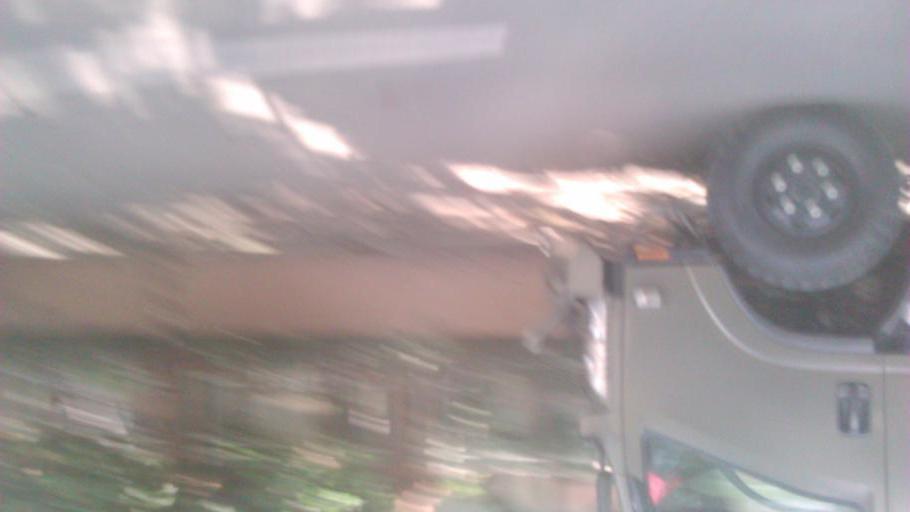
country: ID
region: East Java
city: Pacarkeling
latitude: -7.2560
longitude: 112.7541
